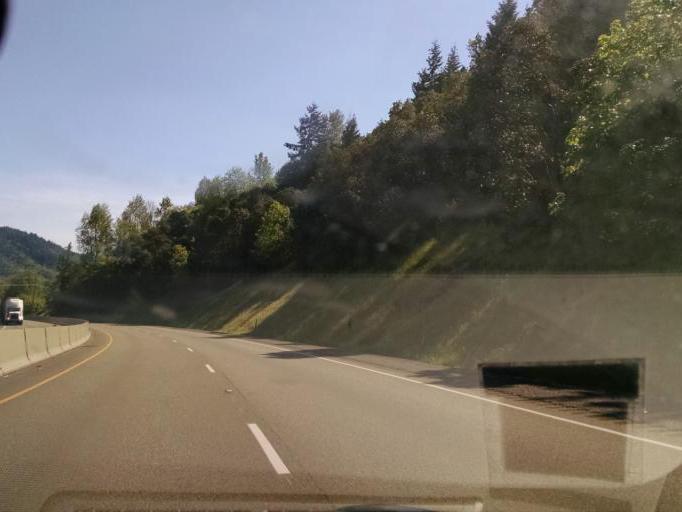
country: US
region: Oregon
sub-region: Douglas County
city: Myrtle Creek
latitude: 43.0190
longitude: -123.3019
